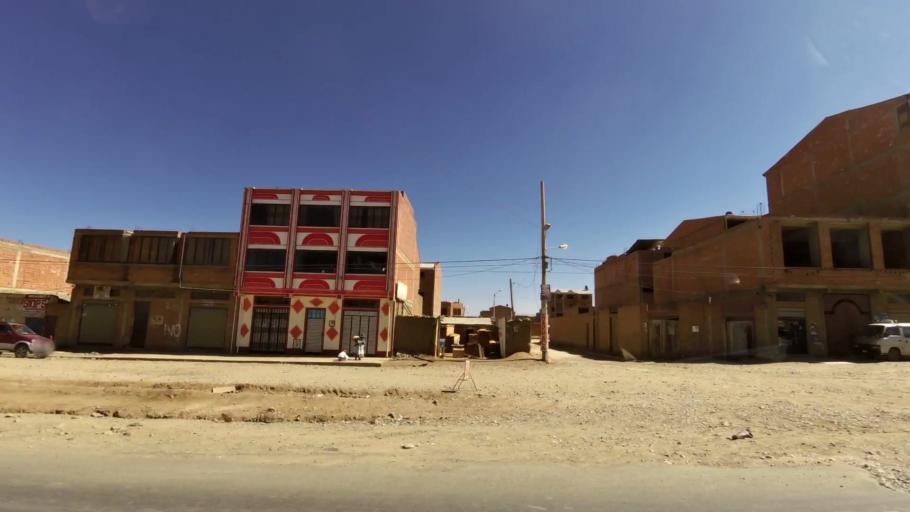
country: BO
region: La Paz
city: La Paz
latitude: -16.5439
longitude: -68.1995
